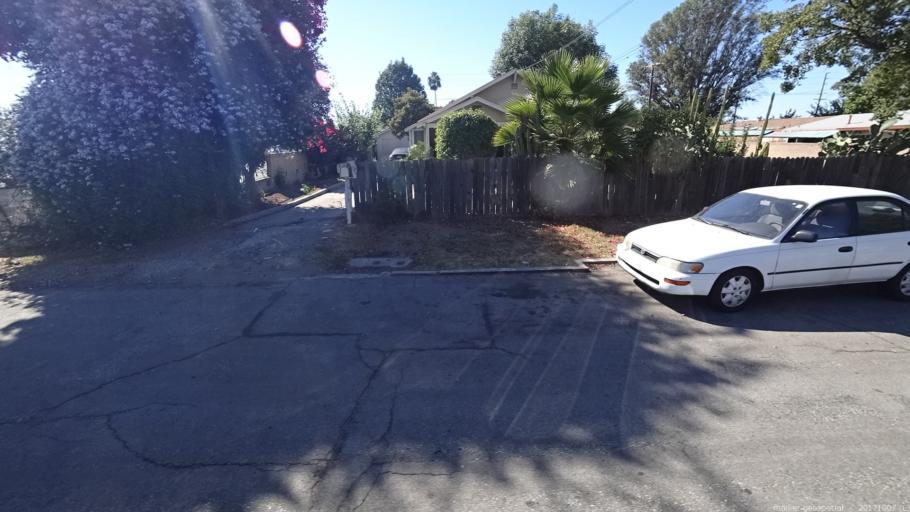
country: US
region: California
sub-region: Orange County
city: Westminster
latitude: 33.7745
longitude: -117.9829
